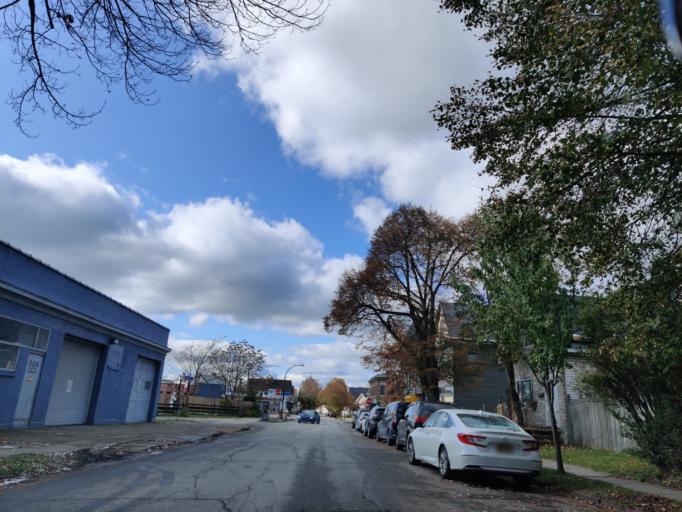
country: US
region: New York
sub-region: Erie County
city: Buffalo
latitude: 42.9114
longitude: -78.8850
